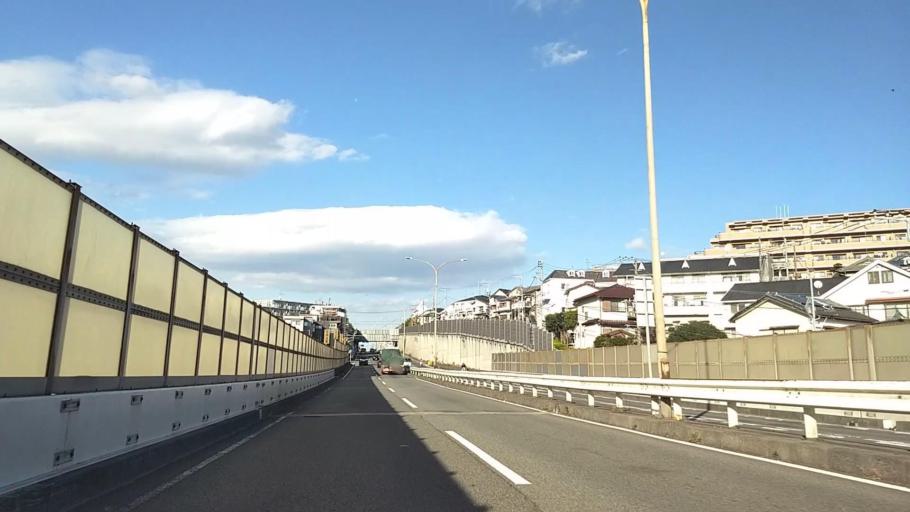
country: JP
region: Tokyo
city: Chofugaoka
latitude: 35.5848
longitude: 139.5986
